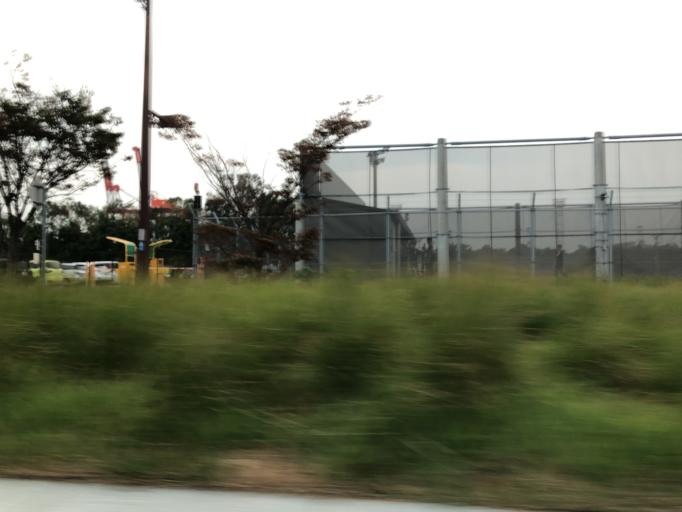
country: JP
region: Hyogo
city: Ashiya
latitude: 34.6815
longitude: 135.2684
